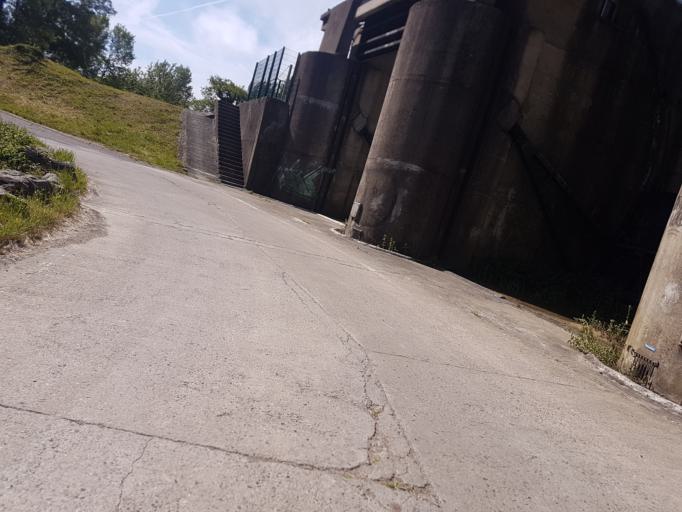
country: FR
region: Rhone-Alpes
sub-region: Departement de l'Ardeche
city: La Voulte-sur-Rhone
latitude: 44.7817
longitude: 4.7736
